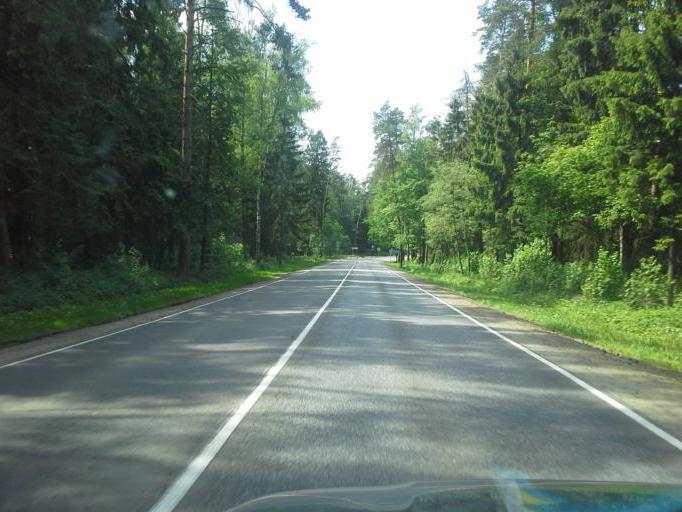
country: RU
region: Moskovskaya
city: Gorki Vtoryye
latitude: 55.7125
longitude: 37.2010
